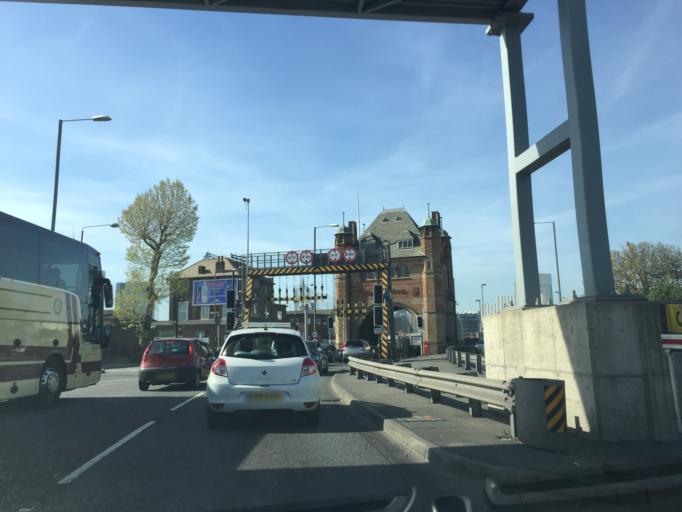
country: GB
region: England
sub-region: Greater London
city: Poplar
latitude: 51.4962
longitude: 0.0024
